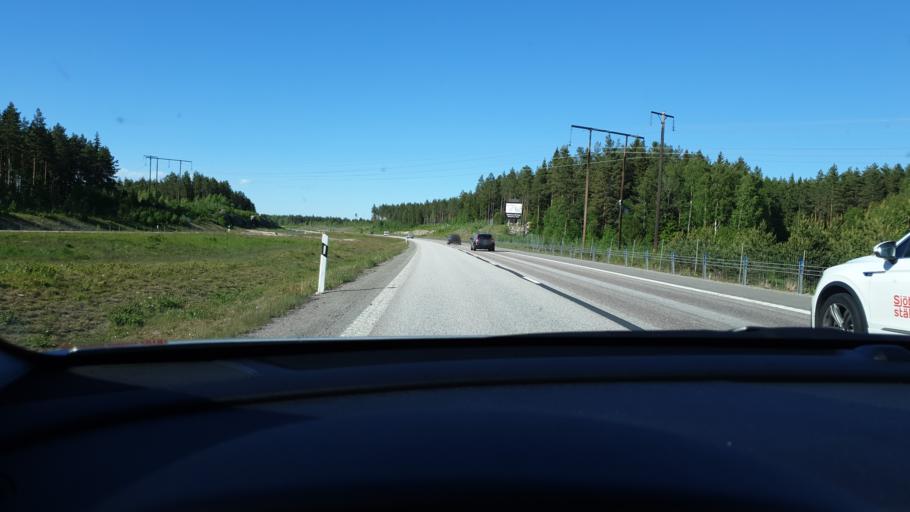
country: SE
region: Uppsala
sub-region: Tierps Kommun
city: Tierp
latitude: 60.2981
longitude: 17.5181
